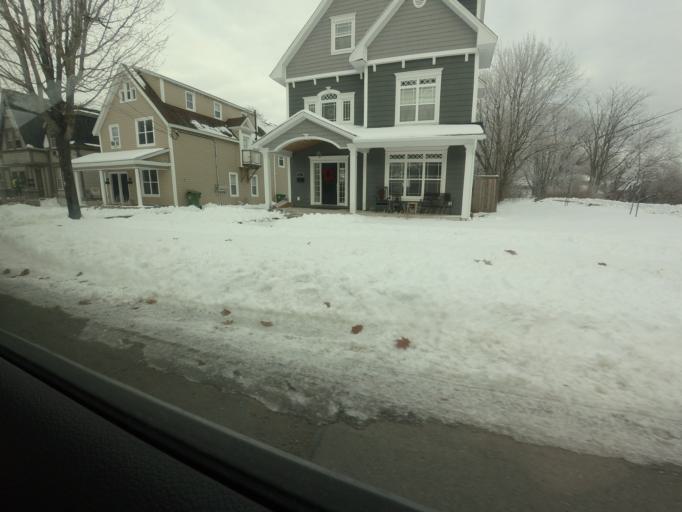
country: CA
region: New Brunswick
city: Fredericton
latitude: 45.9550
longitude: -66.6363
